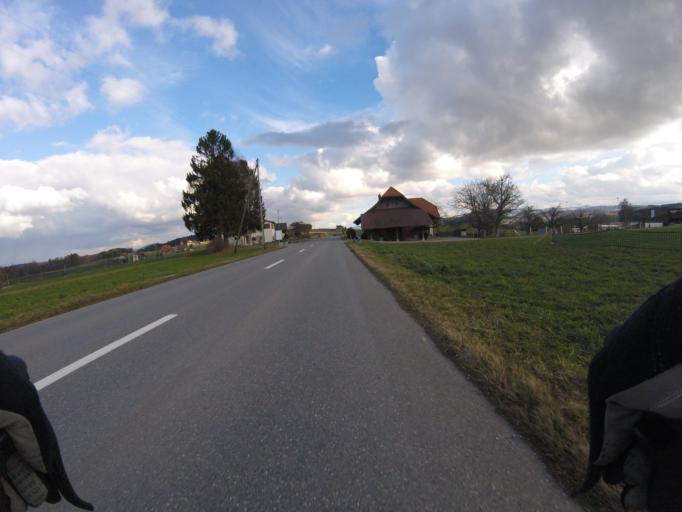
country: CH
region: Bern
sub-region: Bern-Mittelland District
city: Frauenkappelen
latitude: 46.9526
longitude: 7.3477
